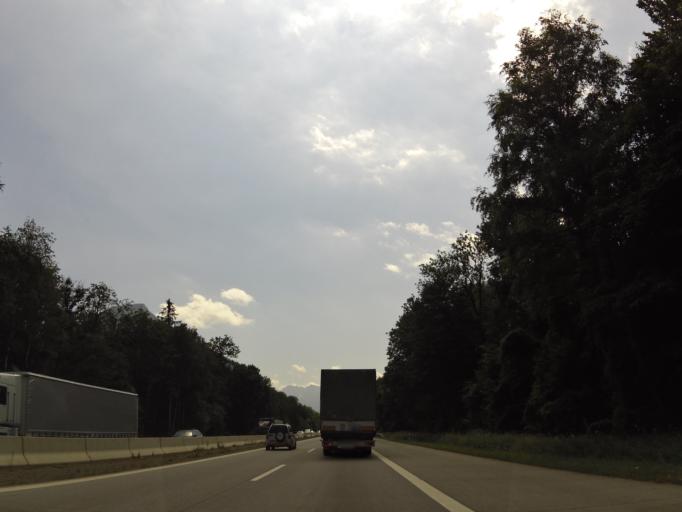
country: DE
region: Bavaria
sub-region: Upper Bavaria
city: Flintsbach
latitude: 47.7180
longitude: 12.1442
